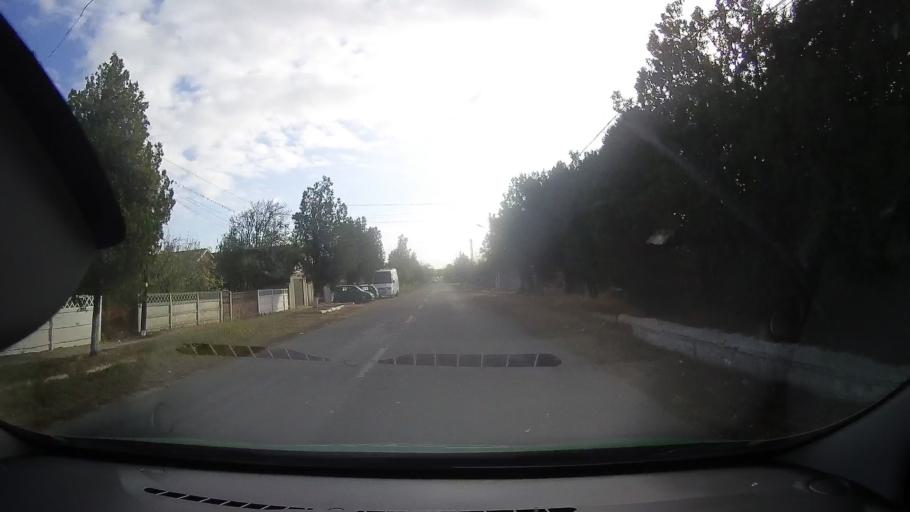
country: RO
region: Constanta
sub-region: Comuna Corbu
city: Corbu
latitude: 44.4113
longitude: 28.6615
